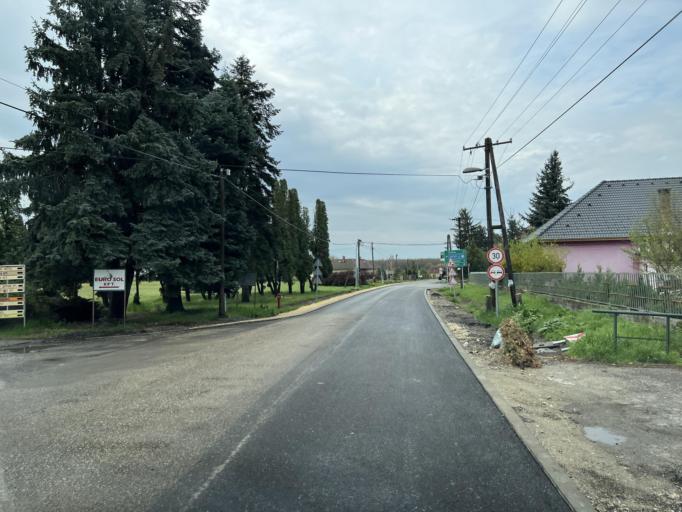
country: HU
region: Pest
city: Danszentmiklos
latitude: 47.2049
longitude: 19.5651
